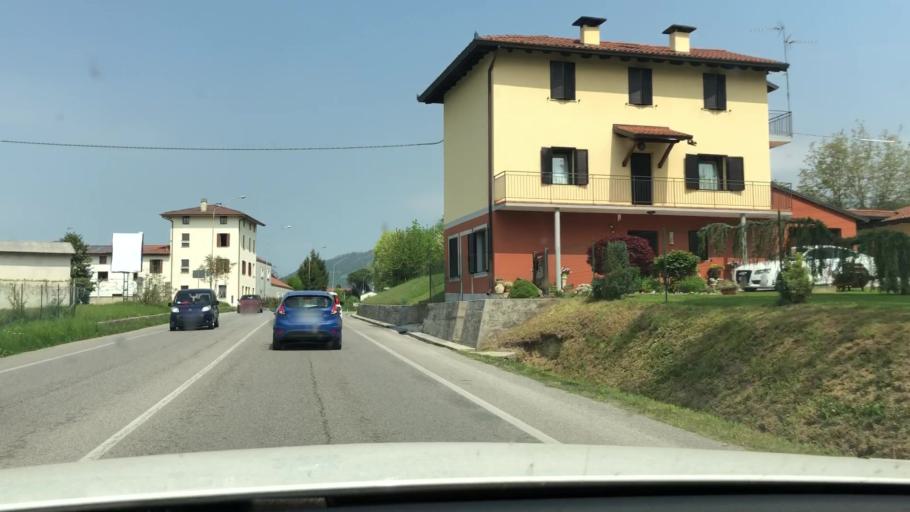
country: IT
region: Friuli Venezia Giulia
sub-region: Provincia di Udine
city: Cassacco
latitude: 46.1958
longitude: 13.1935
